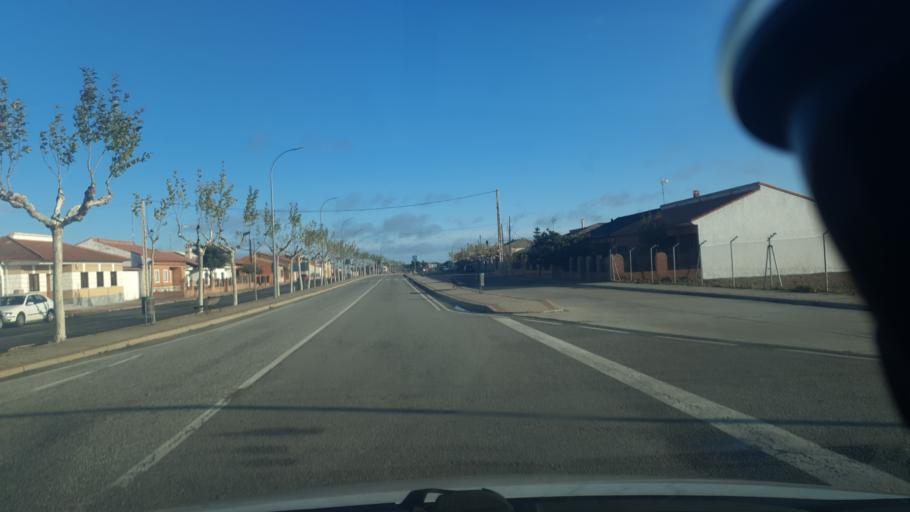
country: ES
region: Castille and Leon
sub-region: Provincia de Avila
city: Tinosillos
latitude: 40.9371
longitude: -4.7261
